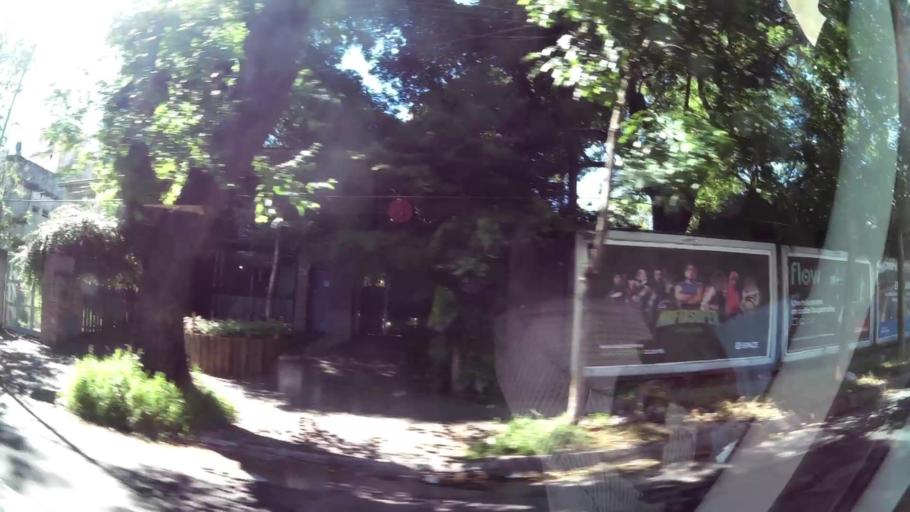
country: AR
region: Buenos Aires
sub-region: Partido de Vicente Lopez
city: Olivos
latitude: -34.5344
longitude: -58.4752
